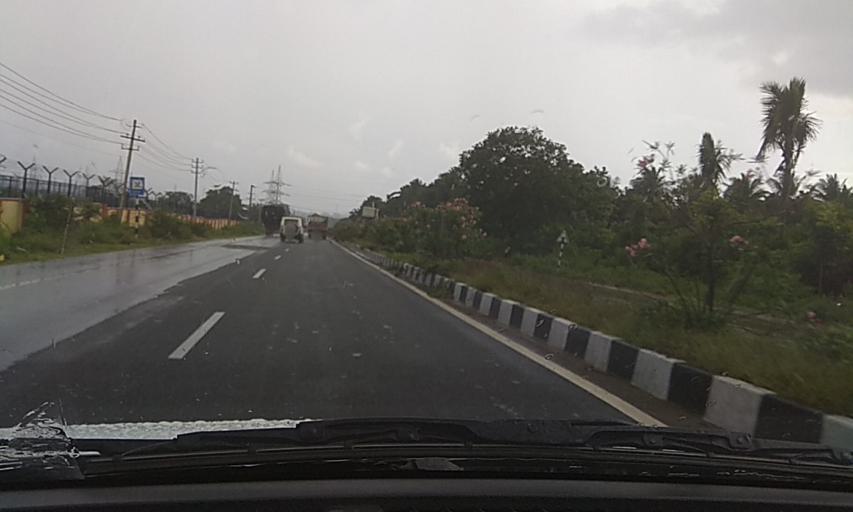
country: IN
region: Karnataka
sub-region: Mysore
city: Nanjangud
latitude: 12.2059
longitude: 76.6648
